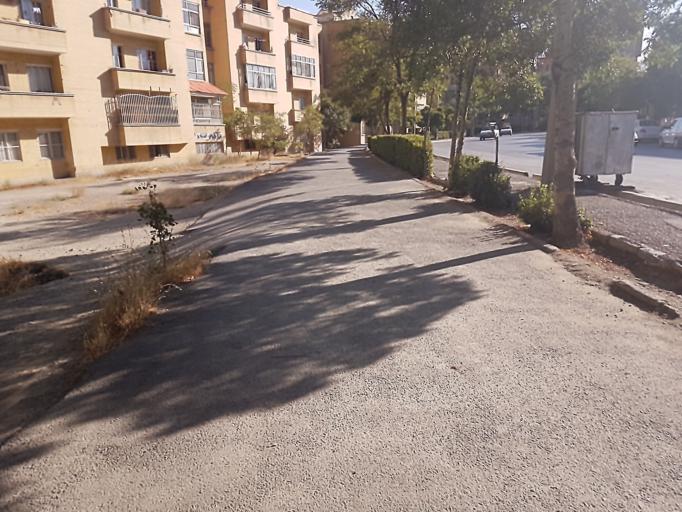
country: IR
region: Markazi
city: Arak
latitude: 34.0691
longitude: 49.6767
